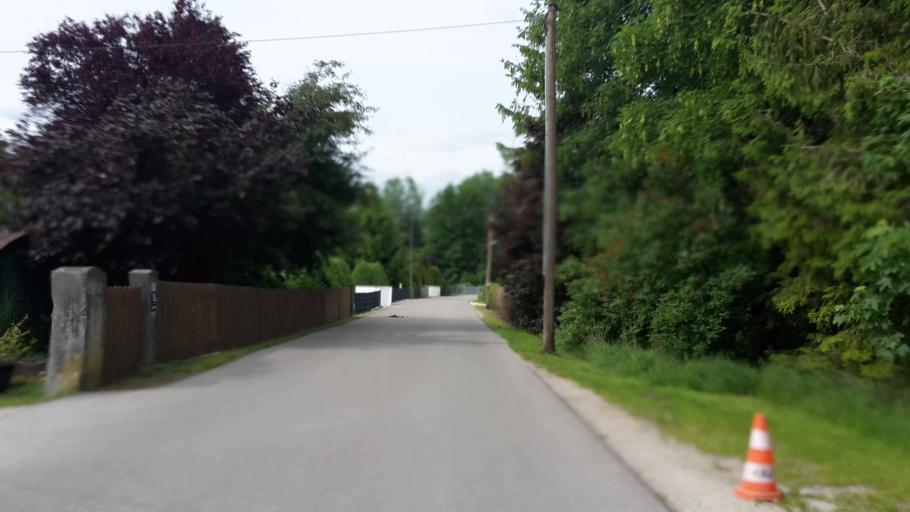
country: DE
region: Bavaria
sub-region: Upper Bavaria
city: Dachau
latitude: 48.2226
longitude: 11.4275
